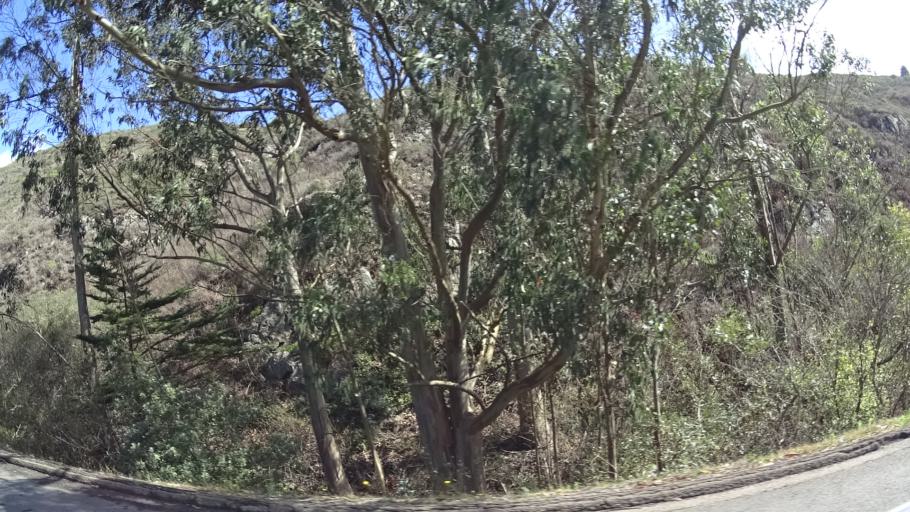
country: US
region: California
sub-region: San Mateo County
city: Daly City
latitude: 37.6990
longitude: -122.4501
